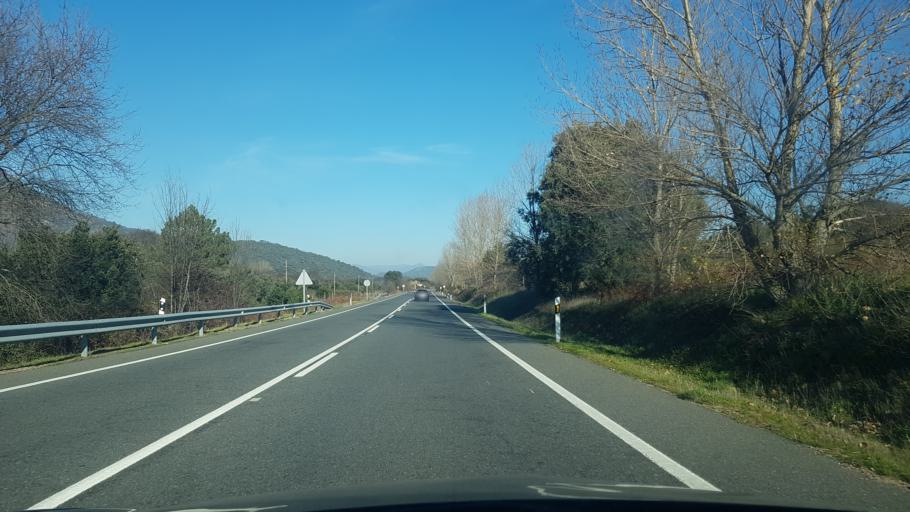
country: ES
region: Madrid
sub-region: Provincia de Madrid
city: Rozas de Puerto Real
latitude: 40.3279
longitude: -4.4751
